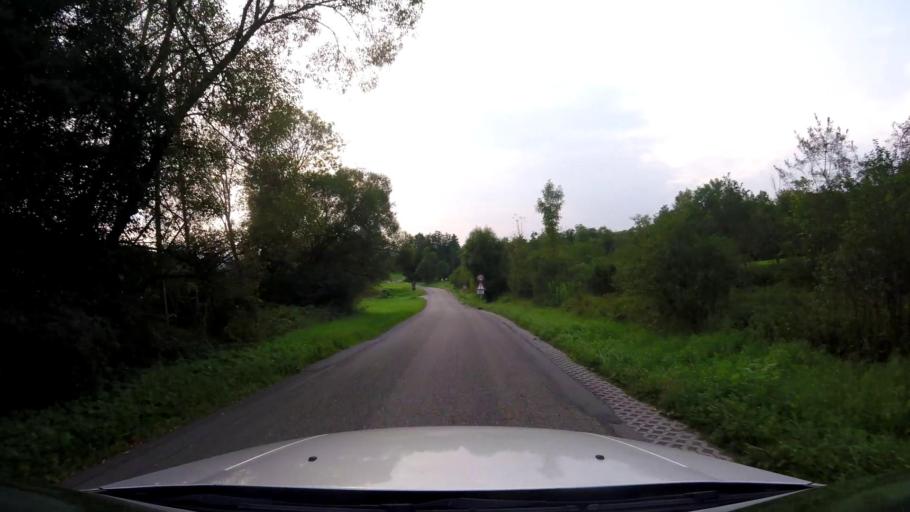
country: DE
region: Baden-Wuerttemberg
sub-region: Regierungsbezirk Stuttgart
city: Rudersberg
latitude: 48.8586
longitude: 9.5616
